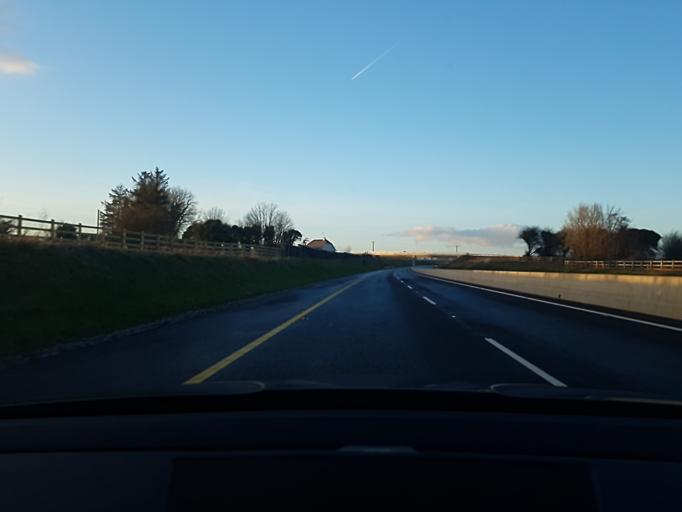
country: IE
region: Connaught
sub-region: County Galway
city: Tuam
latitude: 53.4337
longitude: -8.8433
